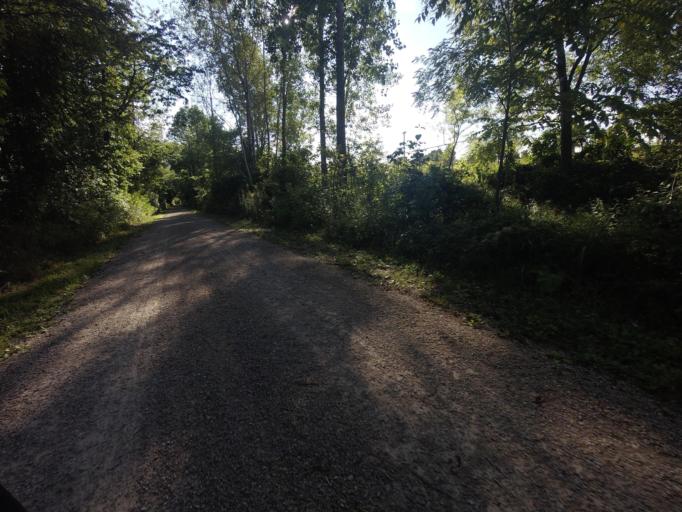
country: CA
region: Ontario
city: Huron East
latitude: 43.7389
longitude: -81.4362
